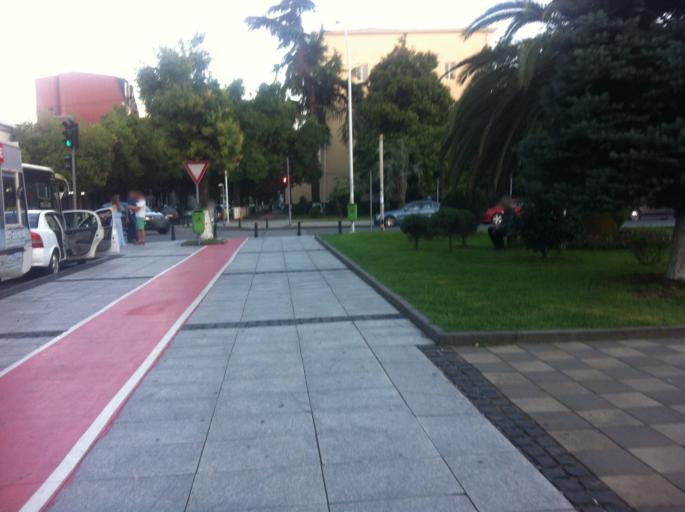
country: GE
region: Ajaria
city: Batumi
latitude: 41.6494
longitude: 41.6354
